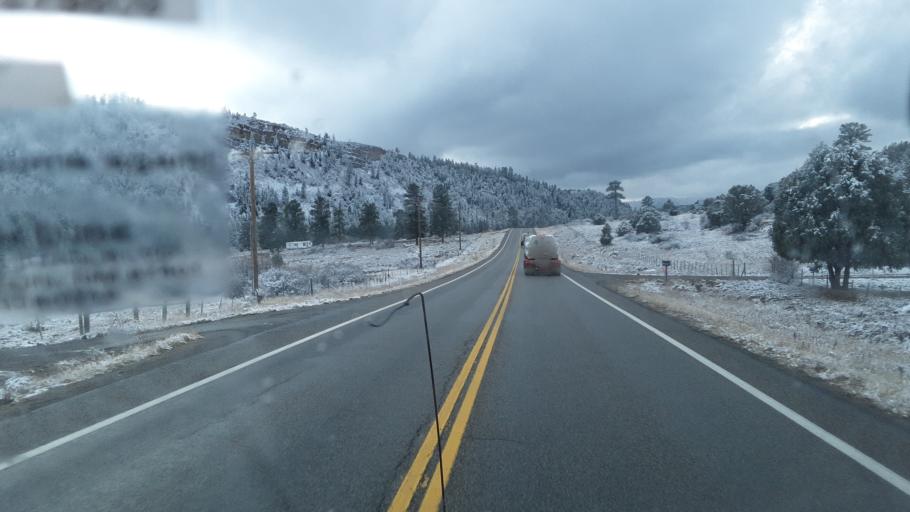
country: US
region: Colorado
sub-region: Archuleta County
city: Pagosa Springs
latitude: 37.2152
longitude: -107.2276
